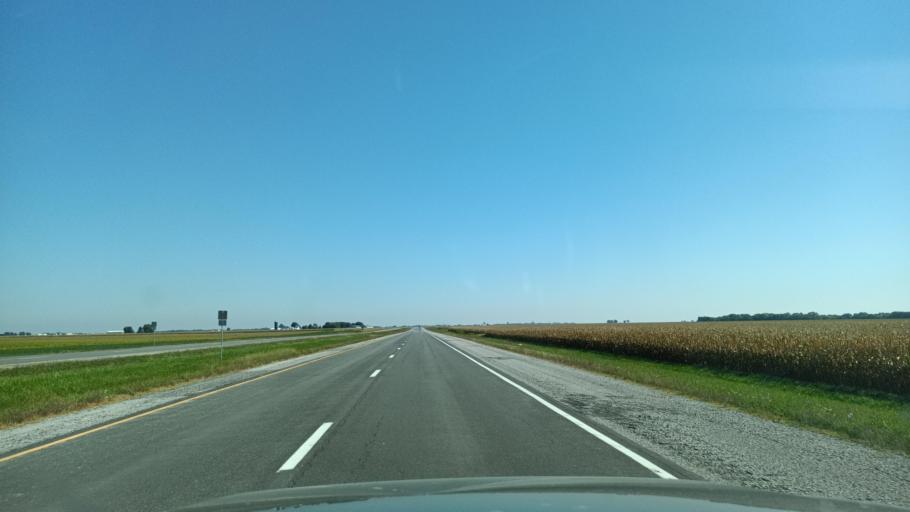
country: US
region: Illinois
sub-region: Adams County
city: Camp Point
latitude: 40.2075
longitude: -91.1374
